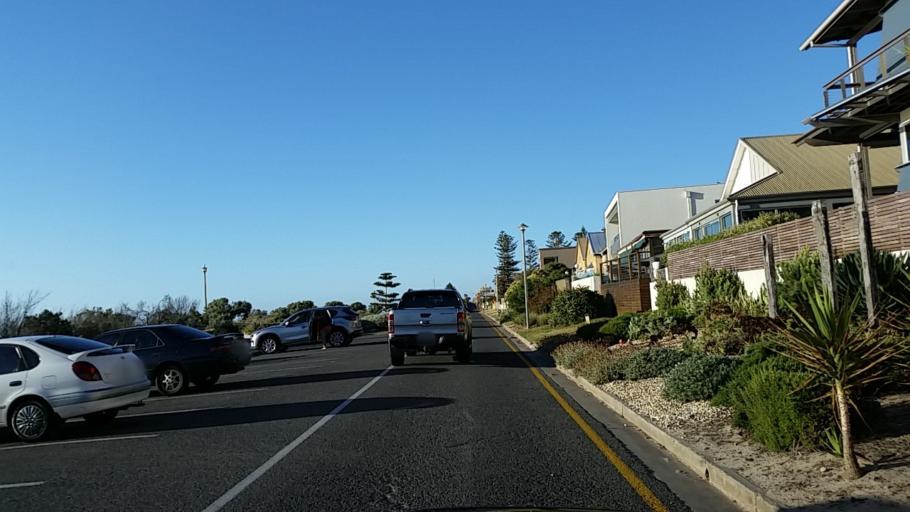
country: AU
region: South Australia
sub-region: Charles Sturt
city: Grange
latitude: -34.9070
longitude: 138.4903
